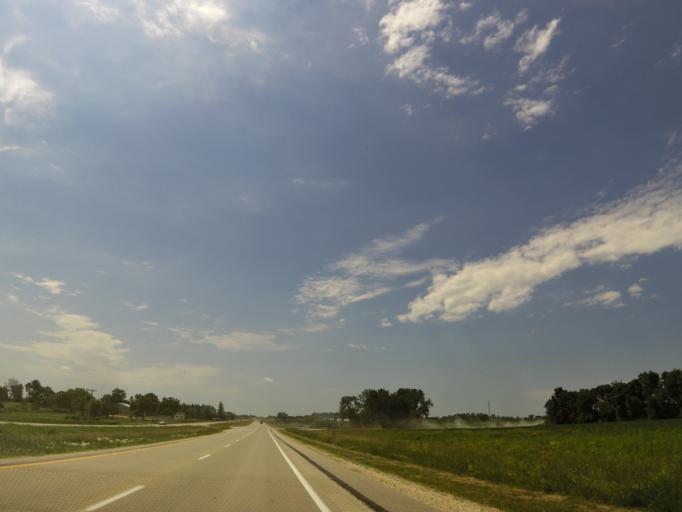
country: US
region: Iowa
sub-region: Bremer County
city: Denver
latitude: 42.7318
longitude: -92.3377
